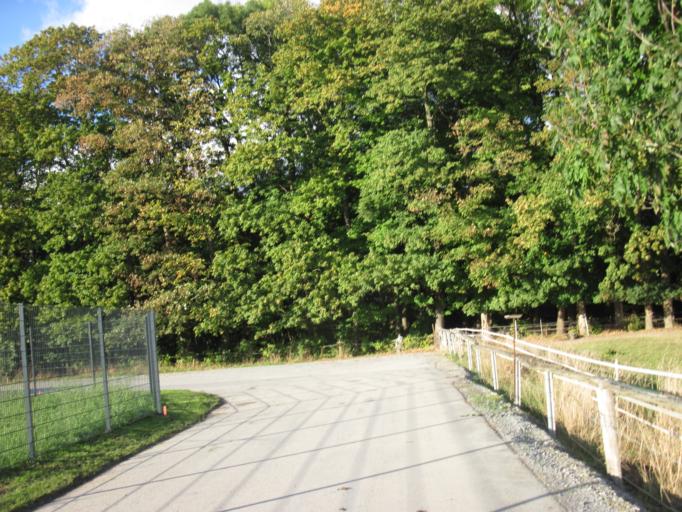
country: DE
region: North Rhine-Westphalia
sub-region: Regierungsbezirk Detmold
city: Paderborn
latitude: 51.7253
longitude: 8.7219
